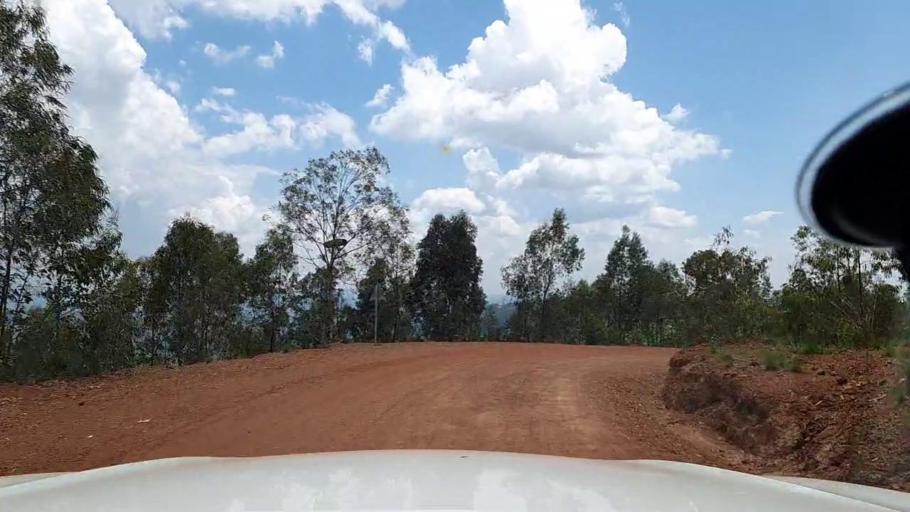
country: RW
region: Kigali
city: Kigali
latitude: -1.7871
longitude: 29.8454
